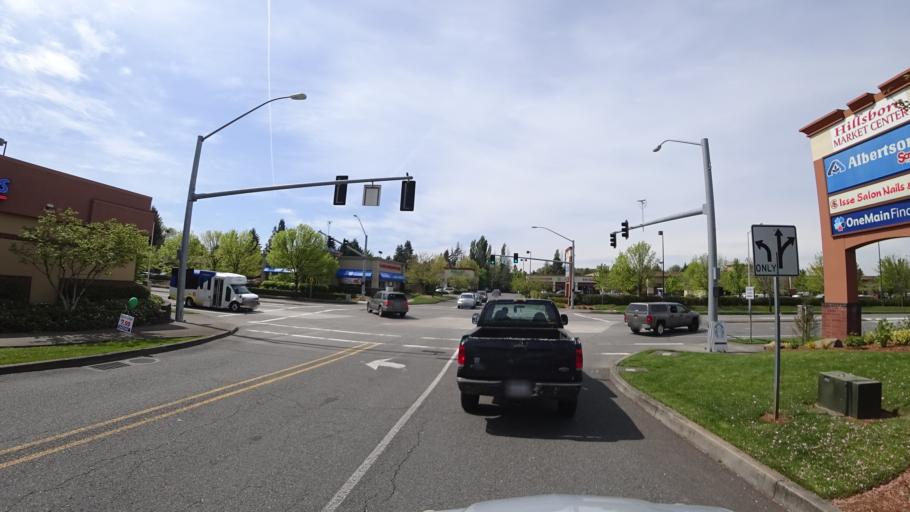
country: US
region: Oregon
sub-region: Washington County
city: Hillsboro
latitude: 45.5297
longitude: -122.9560
